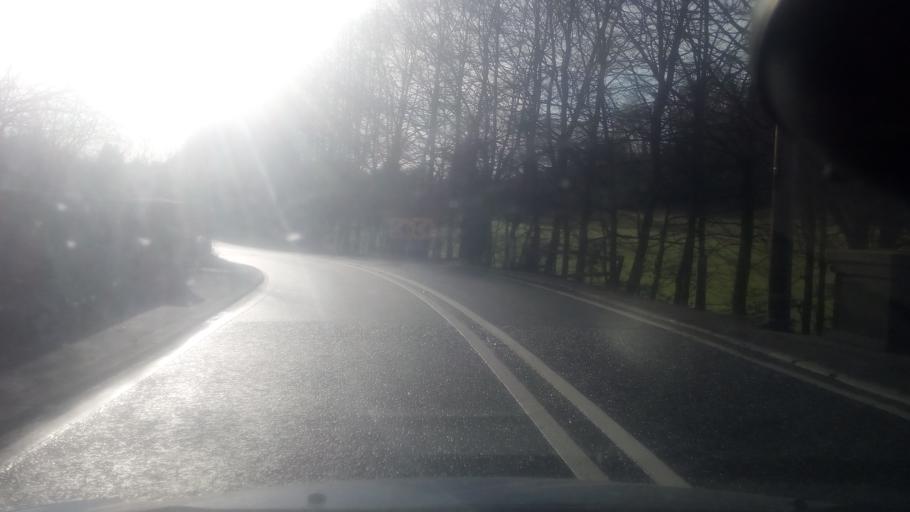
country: GB
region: Scotland
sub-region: The Scottish Borders
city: Jedburgh
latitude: 55.4580
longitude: -2.5586
